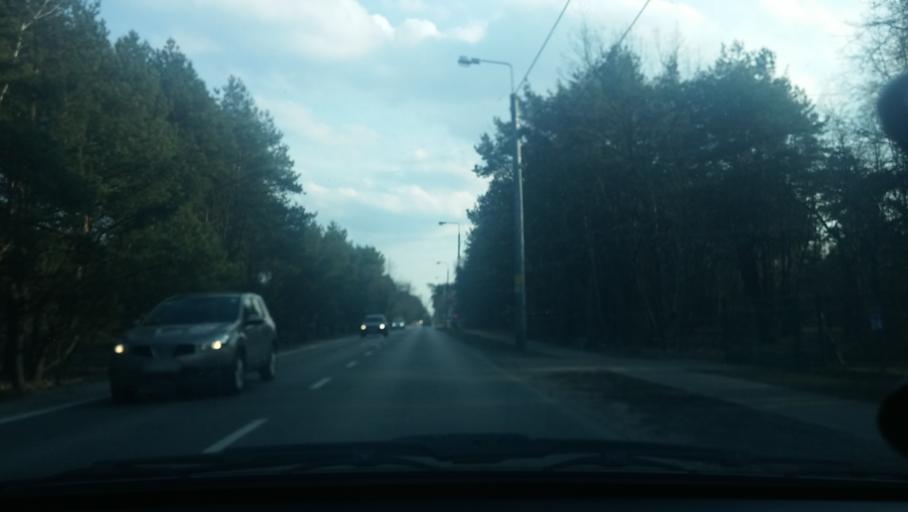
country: PL
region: Masovian Voivodeship
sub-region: Warszawa
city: Wawer
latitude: 52.1694
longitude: 21.2031
